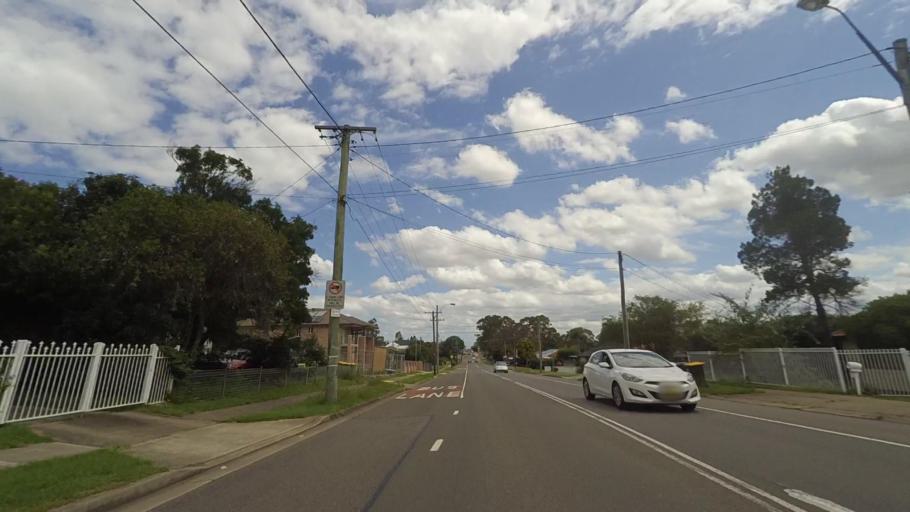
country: AU
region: New South Wales
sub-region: Holroyd
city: Guildford West
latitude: -33.8420
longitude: 150.9635
